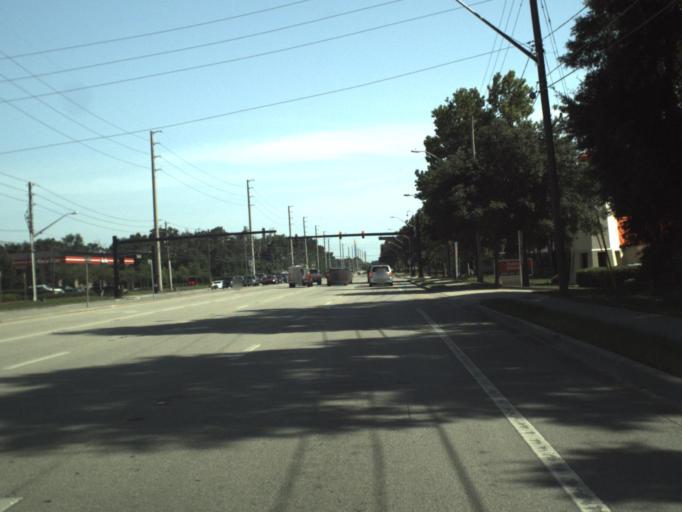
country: US
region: Florida
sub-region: Seminole County
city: Oviedo
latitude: 28.6505
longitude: -81.2083
